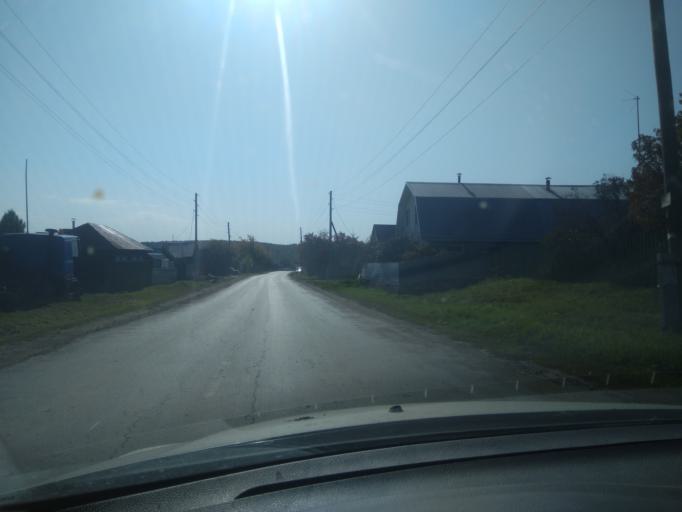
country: RU
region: Sverdlovsk
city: Pokrovskoye
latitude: 56.4411
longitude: 61.6021
